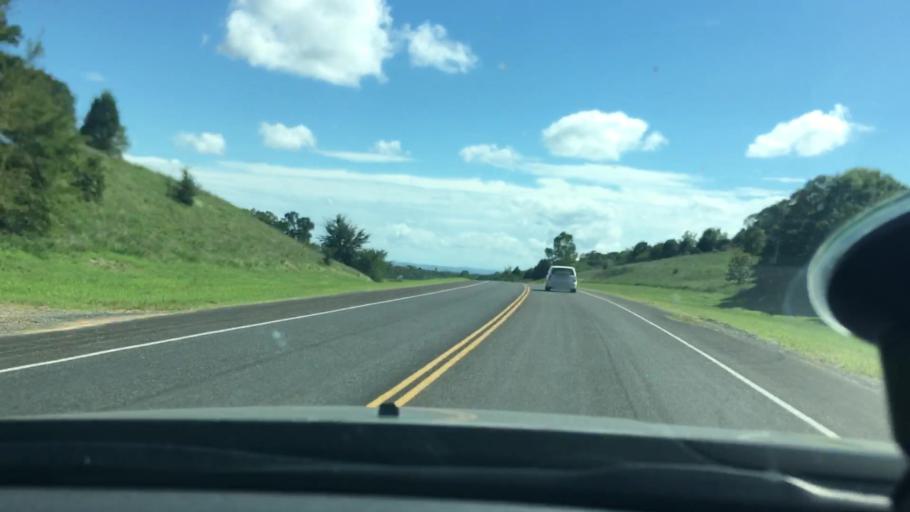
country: US
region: Oklahoma
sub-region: Sequoyah County
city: Vian
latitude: 35.5260
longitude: -94.9745
